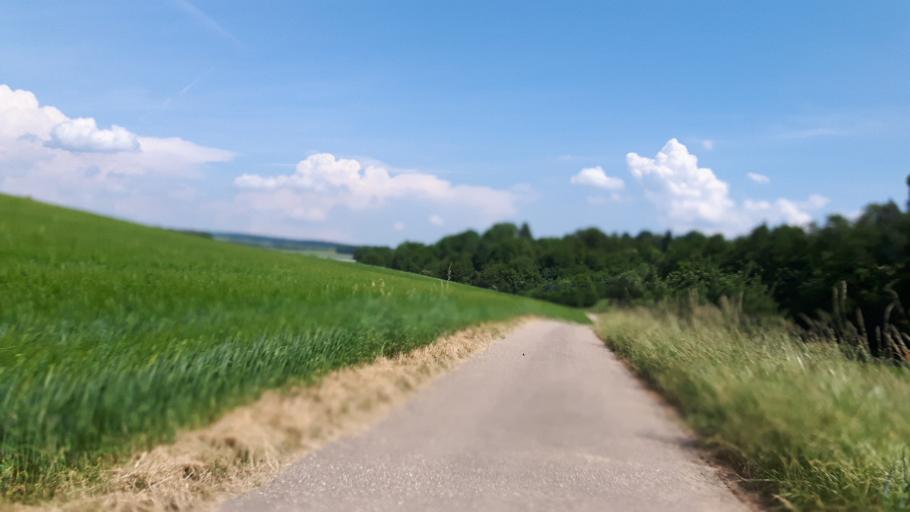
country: DE
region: Baden-Wuerttemberg
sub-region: Regierungsbezirk Stuttgart
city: Neuenstadt am Kocher
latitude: 49.2334
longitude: 9.3115
